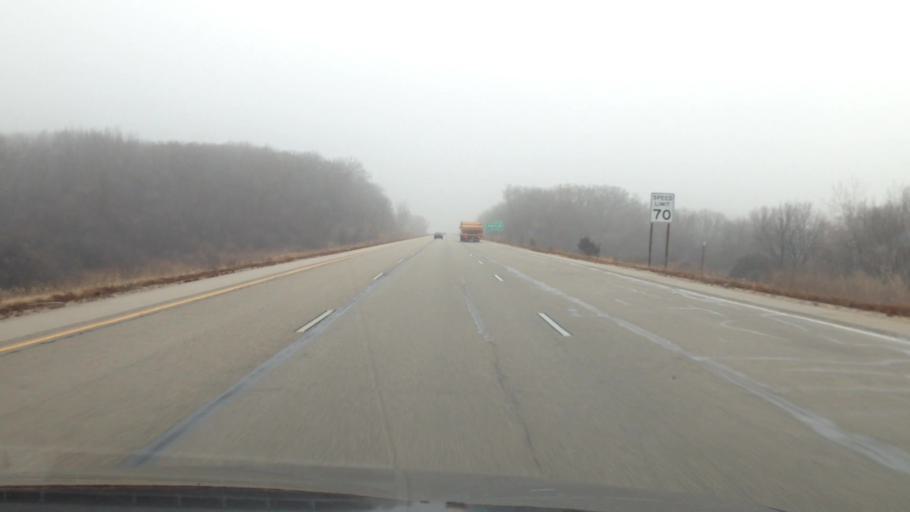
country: US
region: Wisconsin
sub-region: Walworth County
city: East Troy
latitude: 42.7282
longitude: -88.4600
